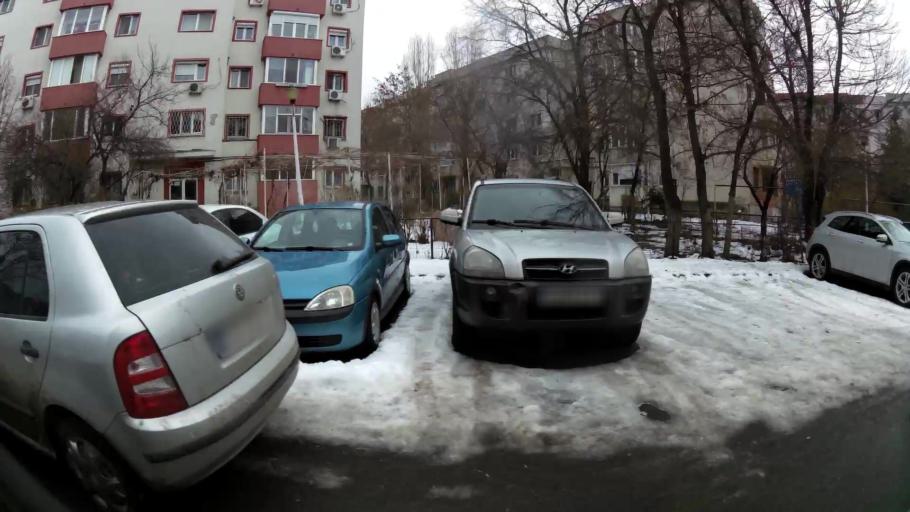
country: RO
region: Bucuresti
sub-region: Municipiul Bucuresti
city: Bucuresti
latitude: 44.4238
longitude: 26.0604
